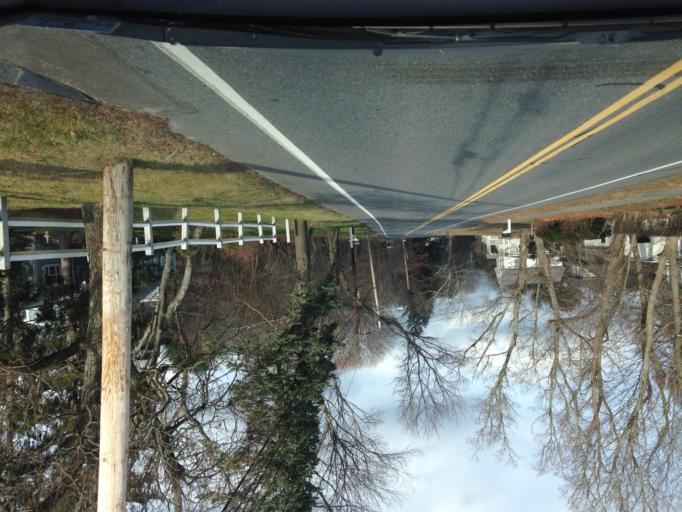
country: US
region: Massachusetts
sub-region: Middlesex County
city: Concord
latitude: 42.4721
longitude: -71.3219
